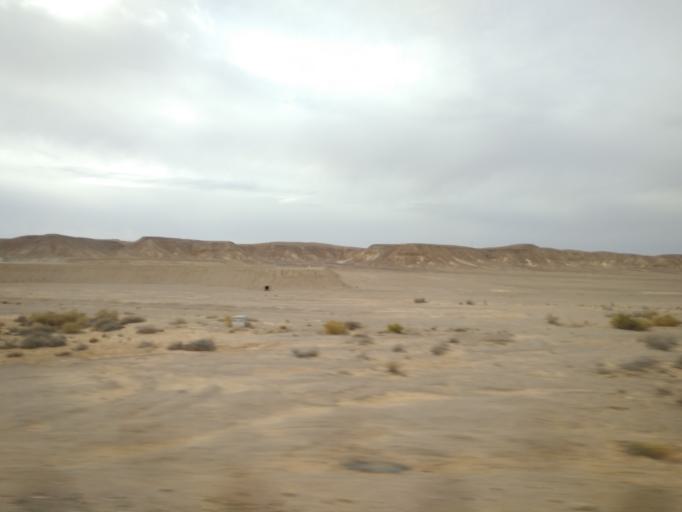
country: IL
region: Southern District
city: Eilat
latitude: 29.9058
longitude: 34.8641
